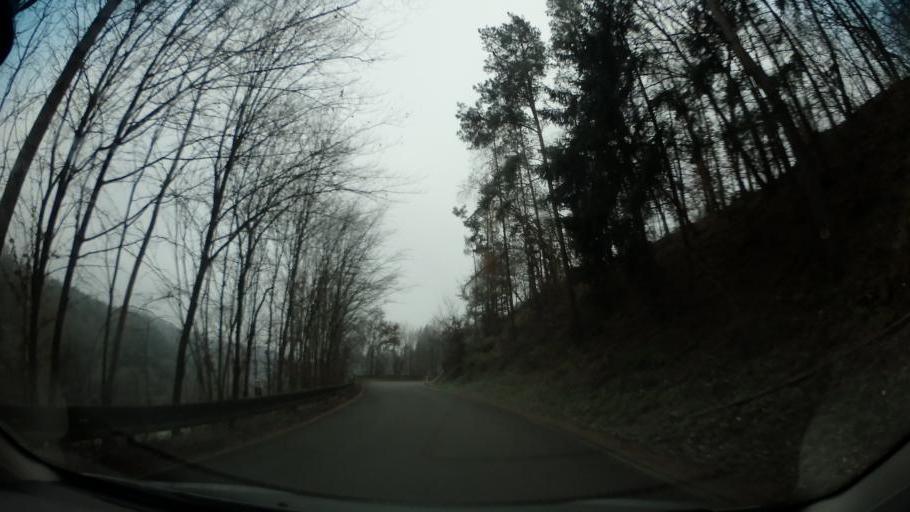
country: CZ
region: Vysocina
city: Mohelno
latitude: 49.1405
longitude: 16.2060
